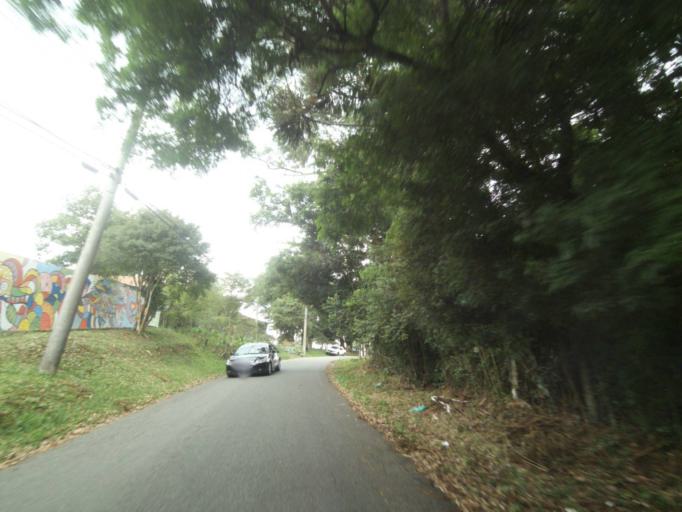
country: BR
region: Parana
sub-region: Curitiba
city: Curitiba
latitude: -25.3998
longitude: -49.2973
